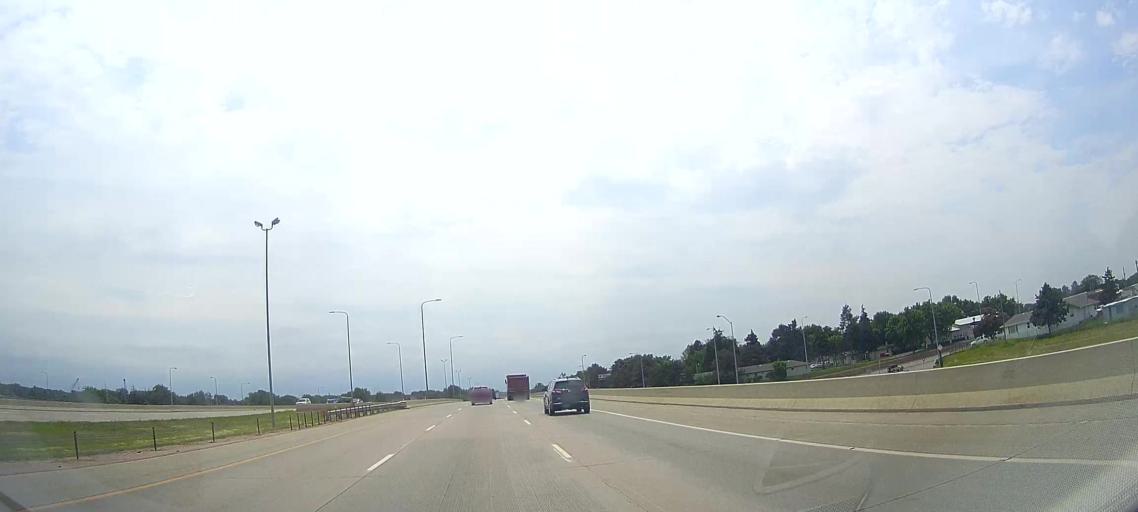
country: US
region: South Dakota
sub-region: Minnehaha County
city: Sioux Falls
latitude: 43.5448
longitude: -96.7805
